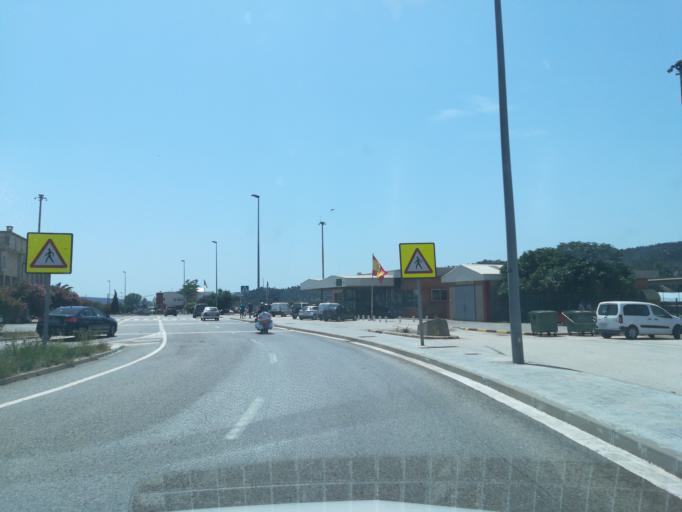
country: ES
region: Catalonia
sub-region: Provincia de Girona
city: la Jonquera
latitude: 42.4304
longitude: 2.8669
